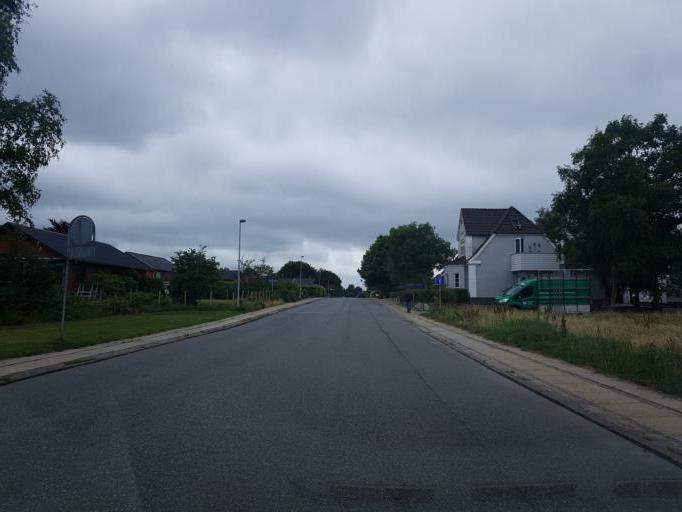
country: DK
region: South Denmark
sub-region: Varde Kommune
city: Varde
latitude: 55.6121
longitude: 8.4750
